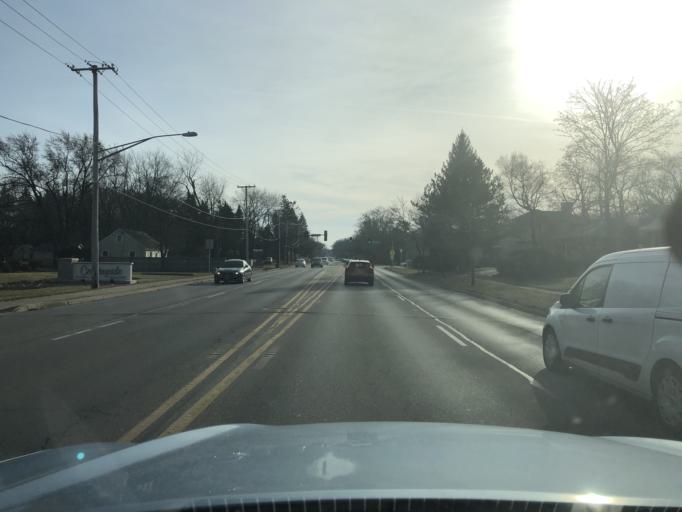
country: US
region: Illinois
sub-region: DuPage County
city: Roselle
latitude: 41.9773
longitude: -88.0804
